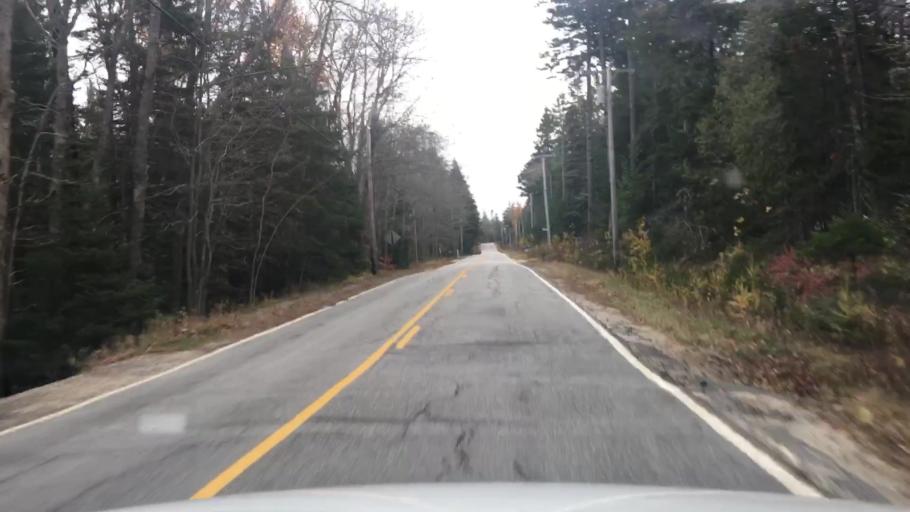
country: US
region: Maine
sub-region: Hancock County
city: Sedgwick
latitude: 44.2997
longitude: -68.5593
